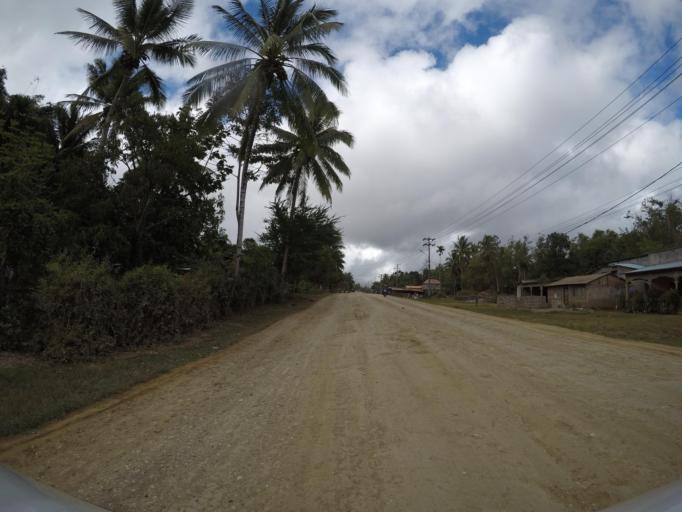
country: TL
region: Lautem
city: Lospalos
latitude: -8.5017
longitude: 126.9900
